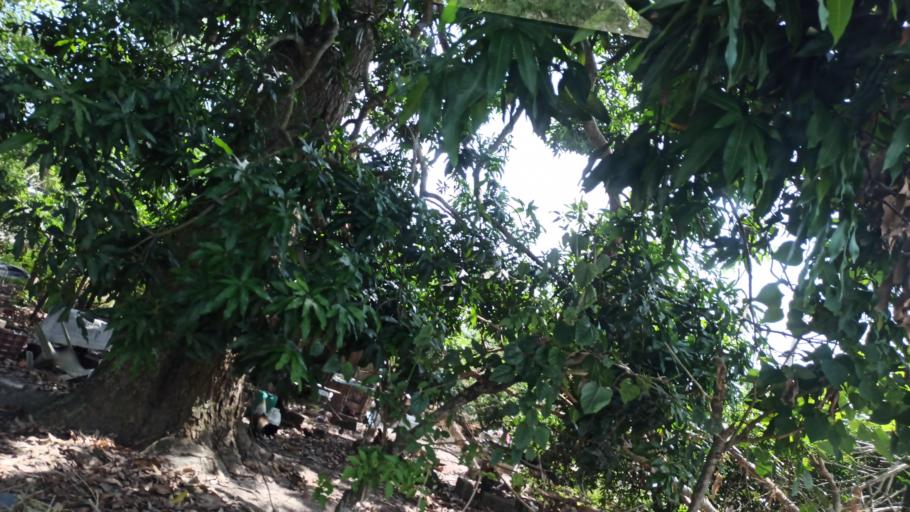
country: MX
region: Puebla
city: San Jose Acateno
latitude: 20.1762
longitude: -97.1130
